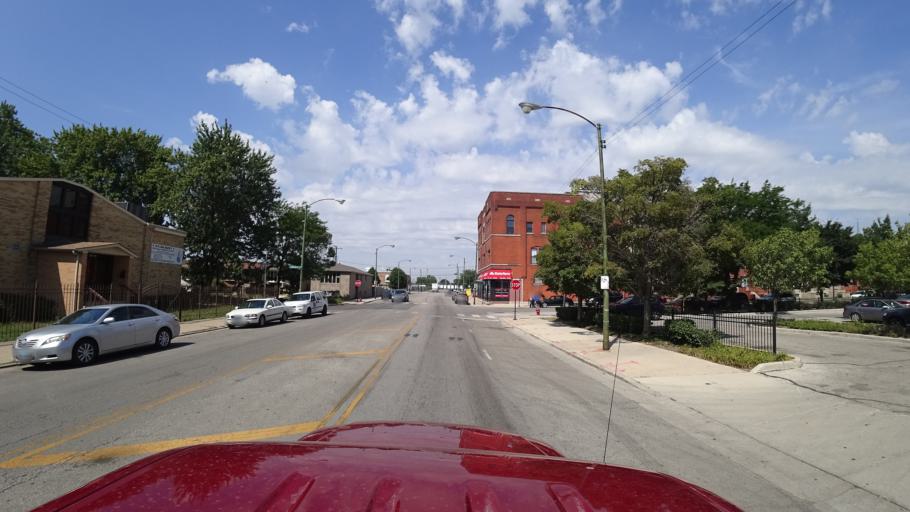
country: US
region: Illinois
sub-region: Cook County
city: Chicago
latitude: 41.8163
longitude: -87.6440
